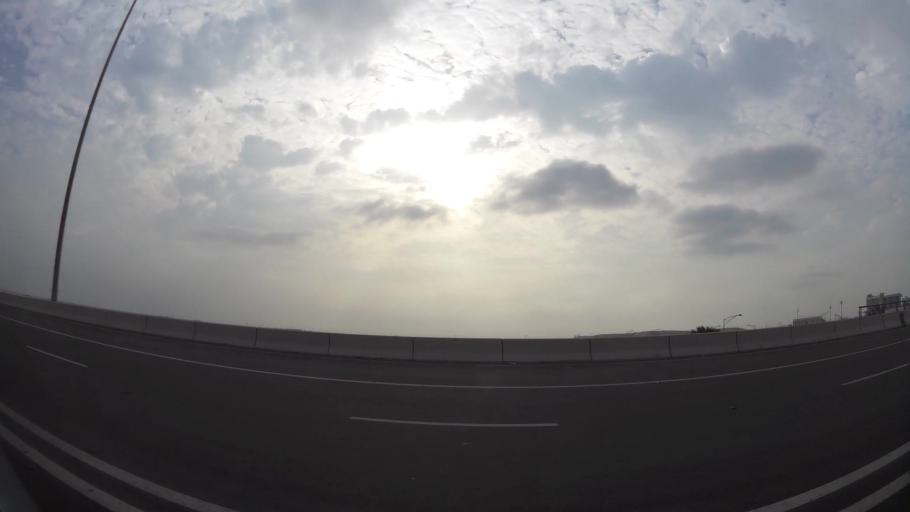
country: AE
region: Abu Dhabi
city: Abu Dhabi
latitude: 24.5337
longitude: 54.4349
